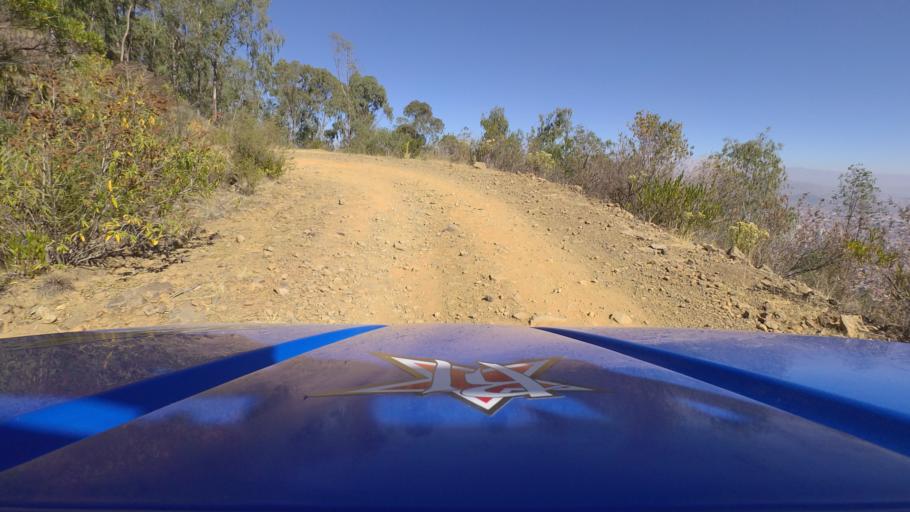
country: BO
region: Cochabamba
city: Cochabamba
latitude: -17.3405
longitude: -66.1492
